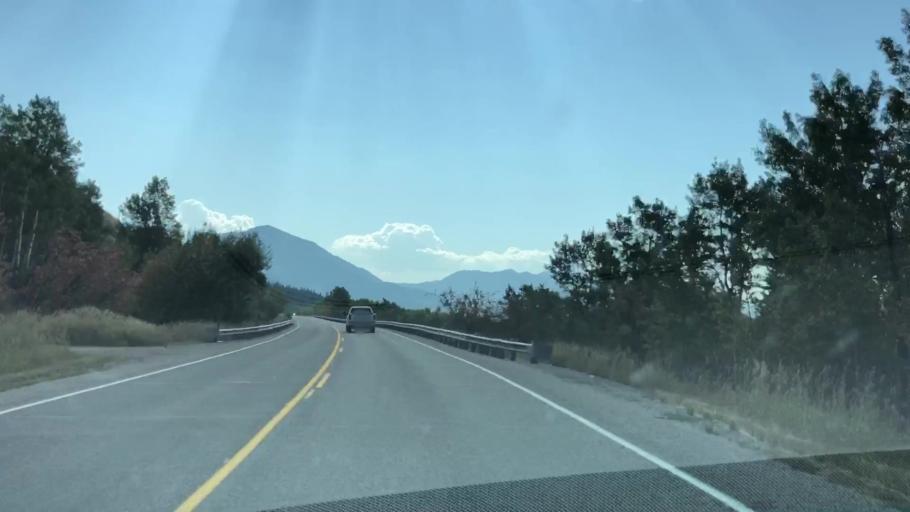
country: US
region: Wyoming
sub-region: Teton County
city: Hoback
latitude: 43.2086
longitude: -111.0567
